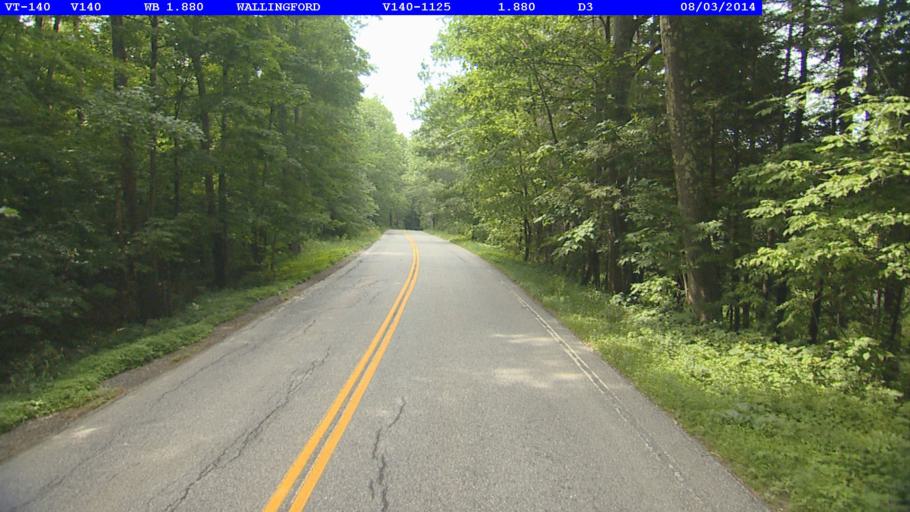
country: US
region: Vermont
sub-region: Rutland County
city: Rutland
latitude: 43.4579
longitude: -72.9480
